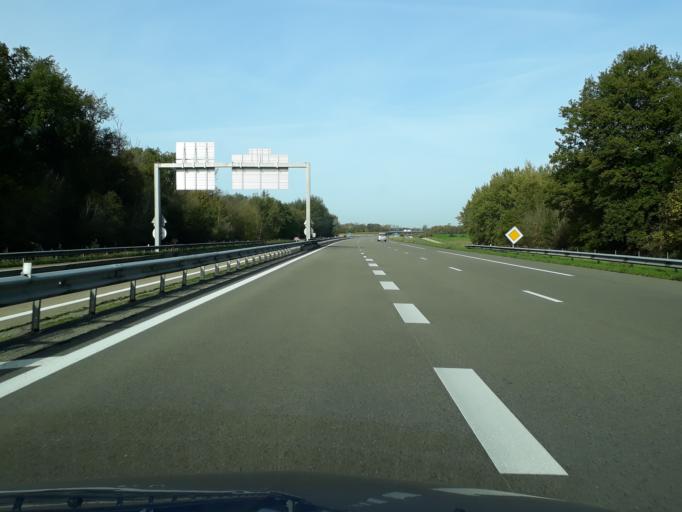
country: FR
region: Champagne-Ardenne
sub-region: Departement de l'Aube
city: Verrieres
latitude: 48.2325
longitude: 4.1772
